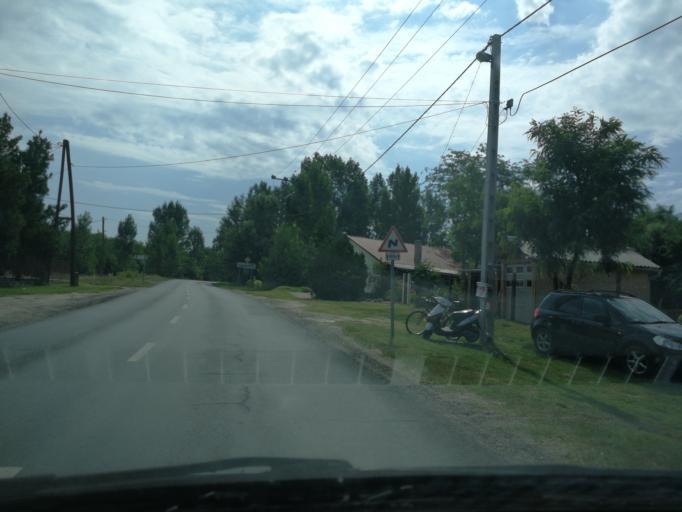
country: HU
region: Bacs-Kiskun
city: Nagybaracska
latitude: 46.0425
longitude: 18.9131
